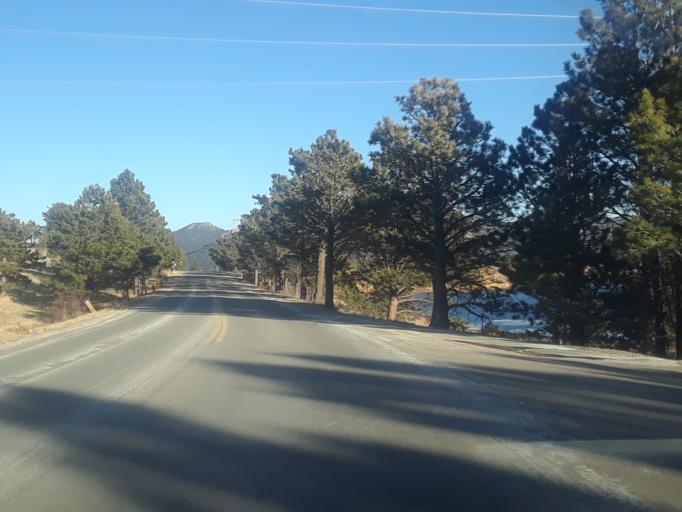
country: US
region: Colorado
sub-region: Larimer County
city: Estes Park
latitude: 40.3471
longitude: -105.5372
